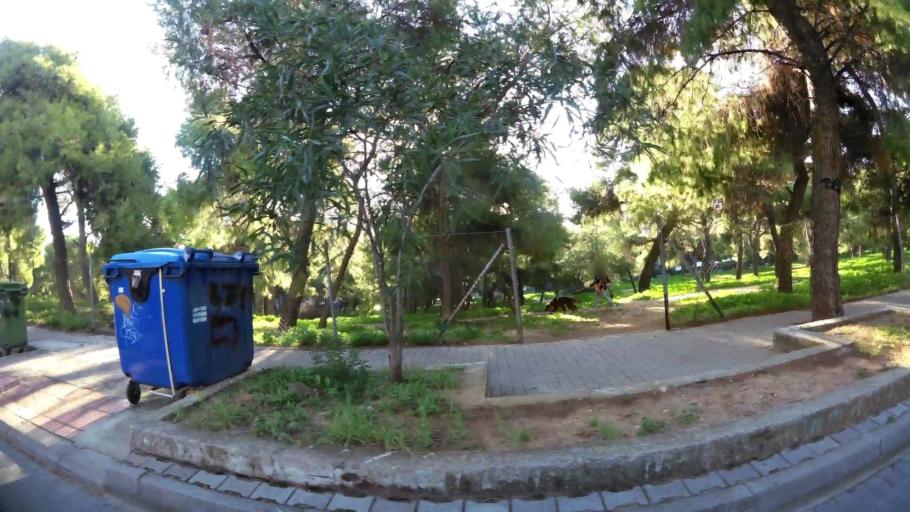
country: GR
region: Attica
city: Pefki
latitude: 38.0547
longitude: 23.7900
